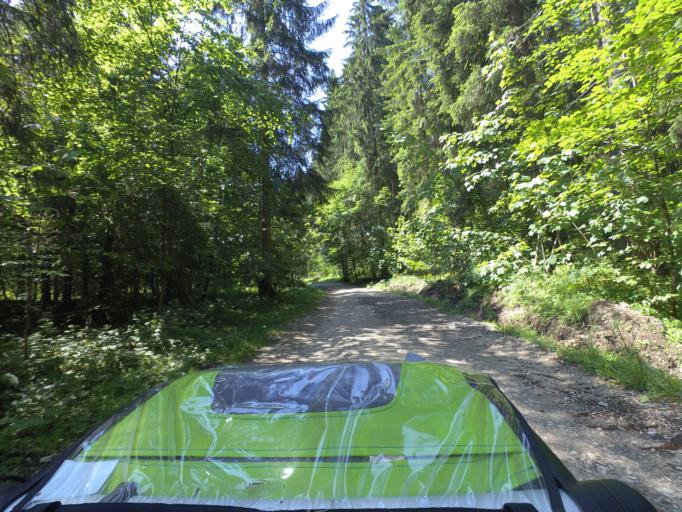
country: DE
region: Bavaria
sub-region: Upper Bavaria
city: Bayerisch Gmain
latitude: 47.7275
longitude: 12.9385
